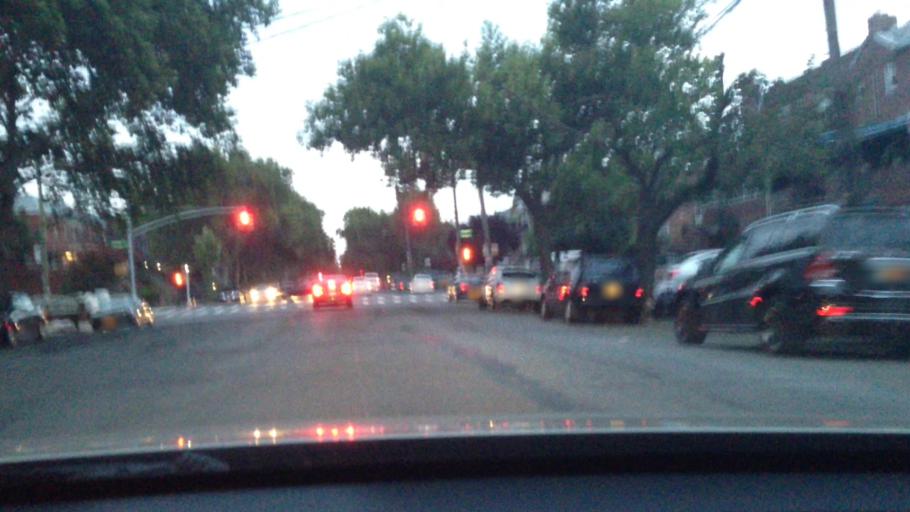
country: US
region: New York
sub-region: Kings County
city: Brooklyn
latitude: 40.6392
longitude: -73.9173
